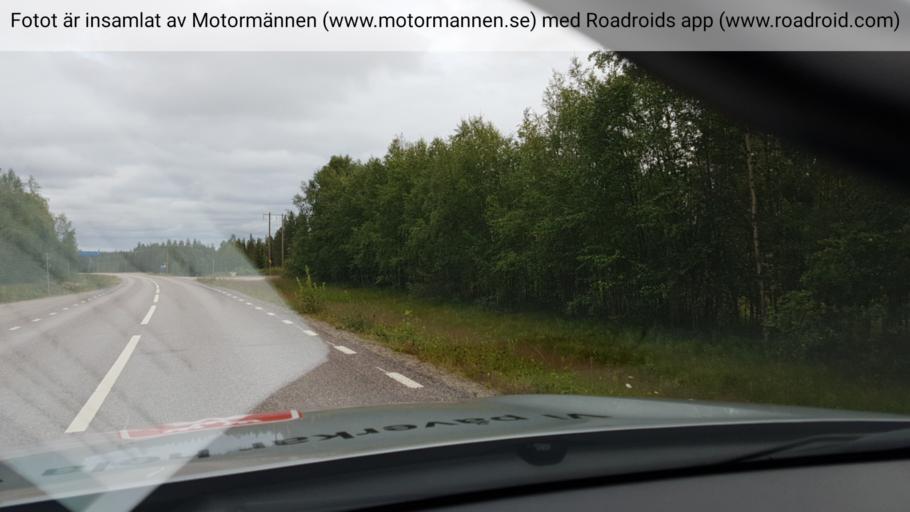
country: SE
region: Norrbotten
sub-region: Gallivare Kommun
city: Gaellivare
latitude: 67.0545
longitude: 21.2363
